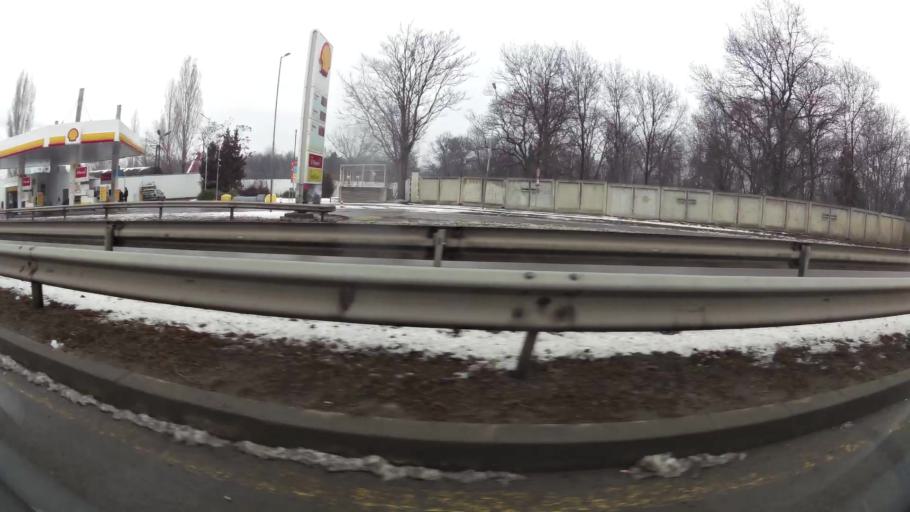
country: BG
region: Sofia-Capital
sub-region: Stolichna Obshtina
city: Sofia
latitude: 42.7139
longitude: 23.3281
